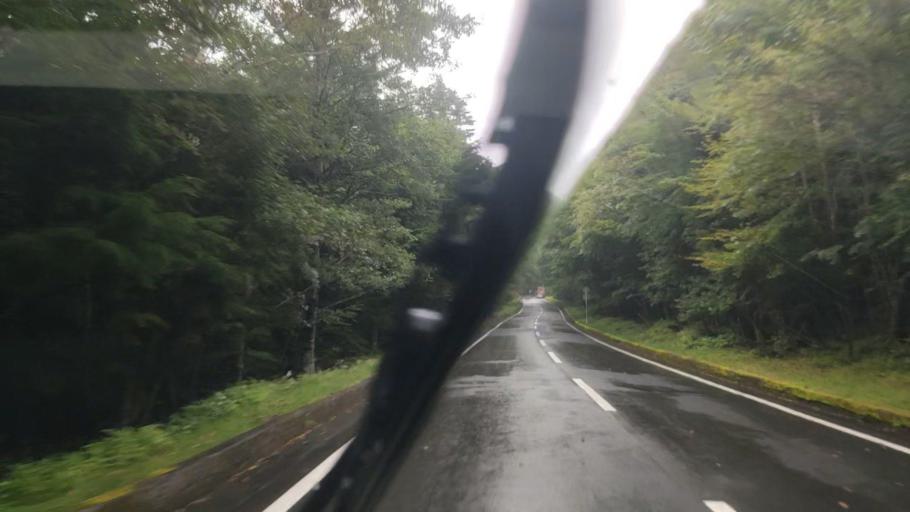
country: JP
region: Shizuoka
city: Fujinomiya
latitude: 35.3228
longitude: 138.7205
